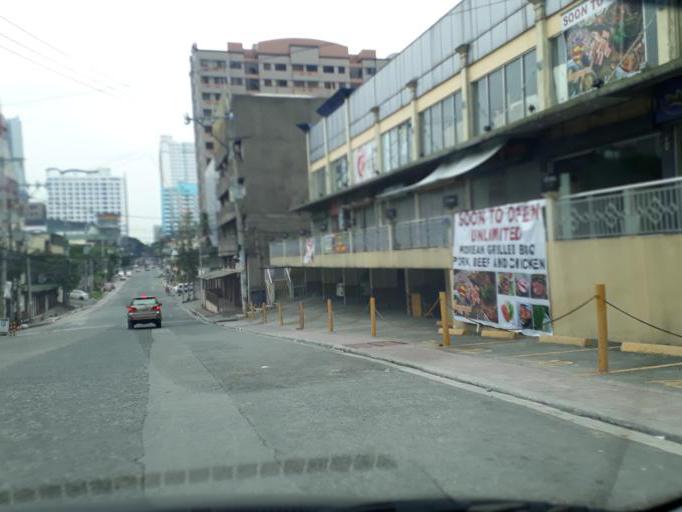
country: PH
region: Calabarzon
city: Del Monte
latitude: 14.6368
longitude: 121.0281
